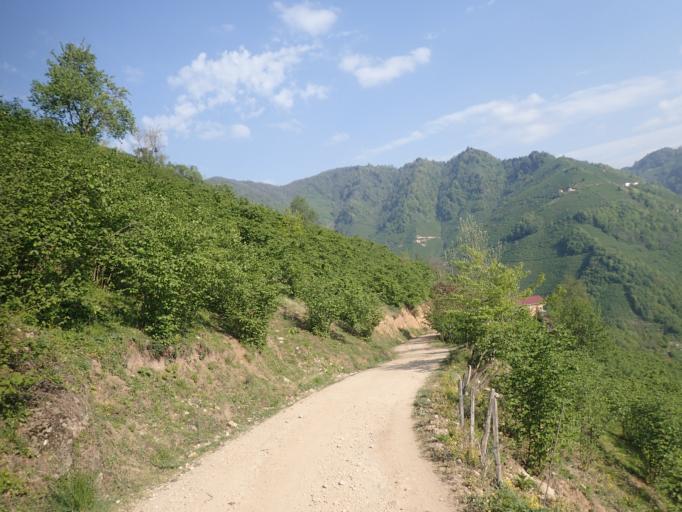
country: TR
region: Ordu
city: Kabaduz
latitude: 40.7938
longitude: 37.8823
